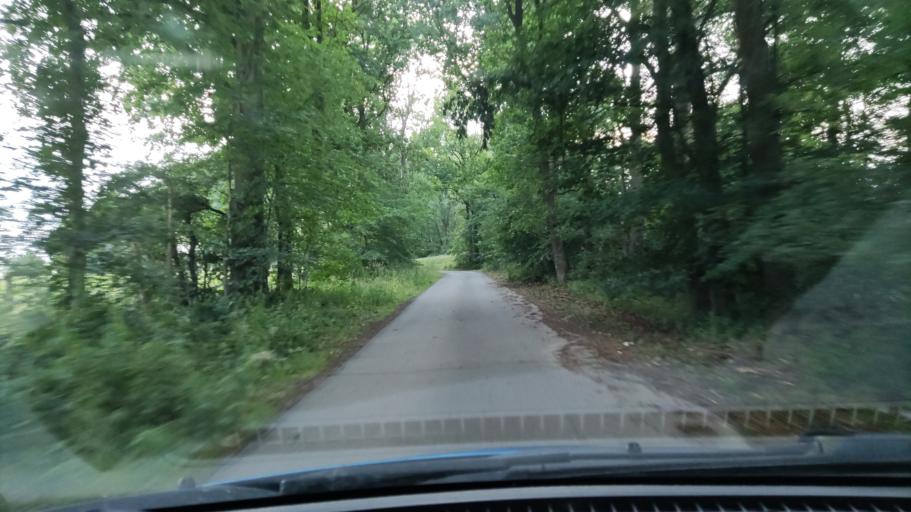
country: DE
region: Lower Saxony
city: Amelinghausen
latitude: 53.1311
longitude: 10.2513
